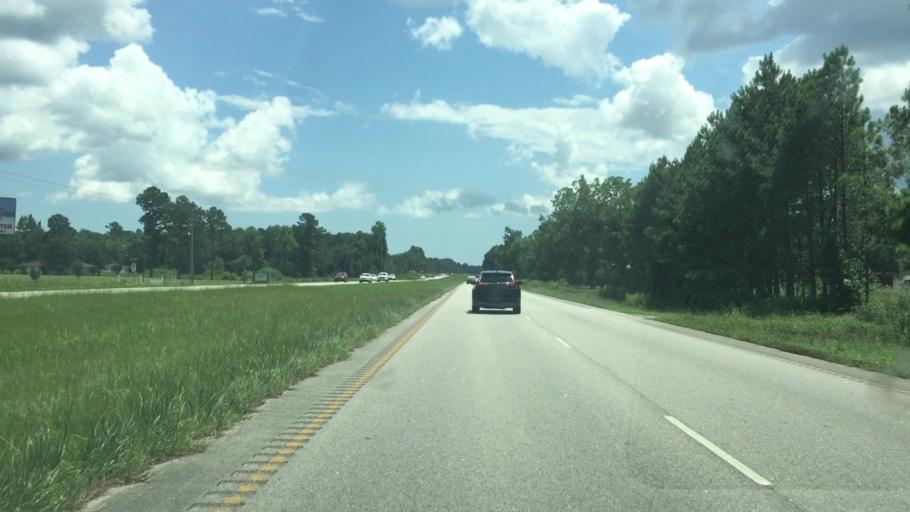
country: US
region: South Carolina
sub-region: Horry County
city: Little River
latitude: 33.9709
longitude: -78.7411
